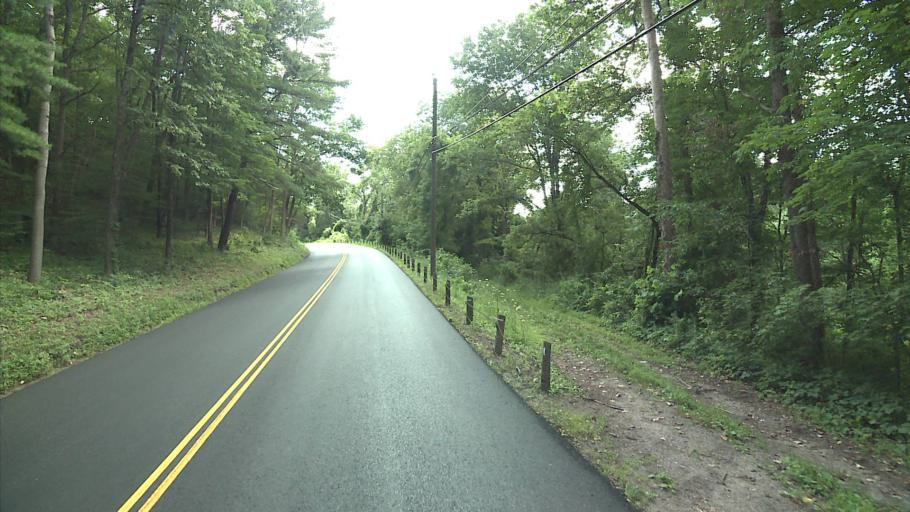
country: US
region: Connecticut
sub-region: Litchfield County
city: Canaan
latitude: 41.9782
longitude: -73.3602
